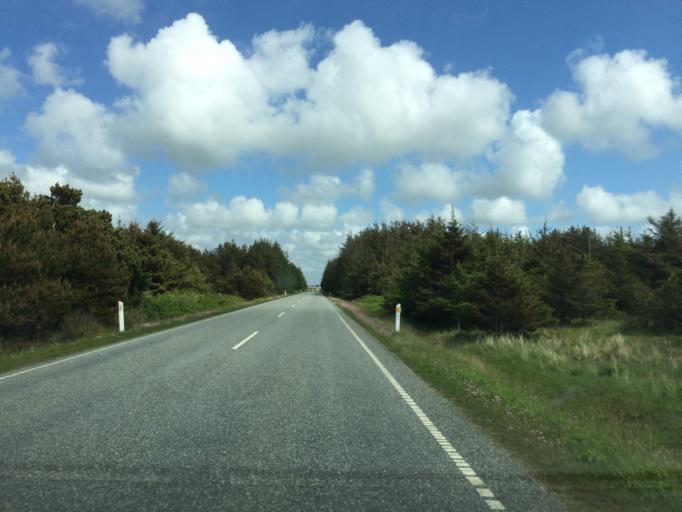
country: DK
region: Central Jutland
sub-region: Holstebro Kommune
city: Ulfborg
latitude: 56.3212
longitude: 8.1302
